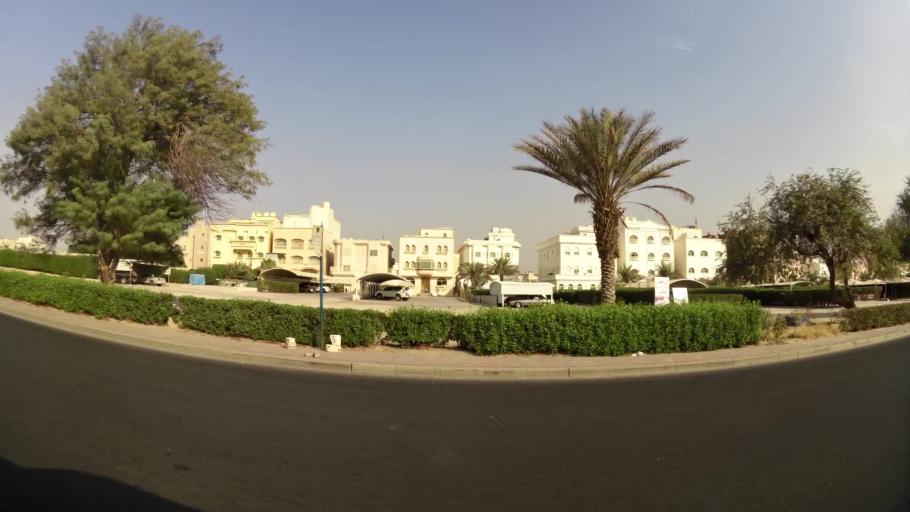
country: KW
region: Mubarak al Kabir
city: Mubarak al Kabir
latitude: 29.1799
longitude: 48.0792
